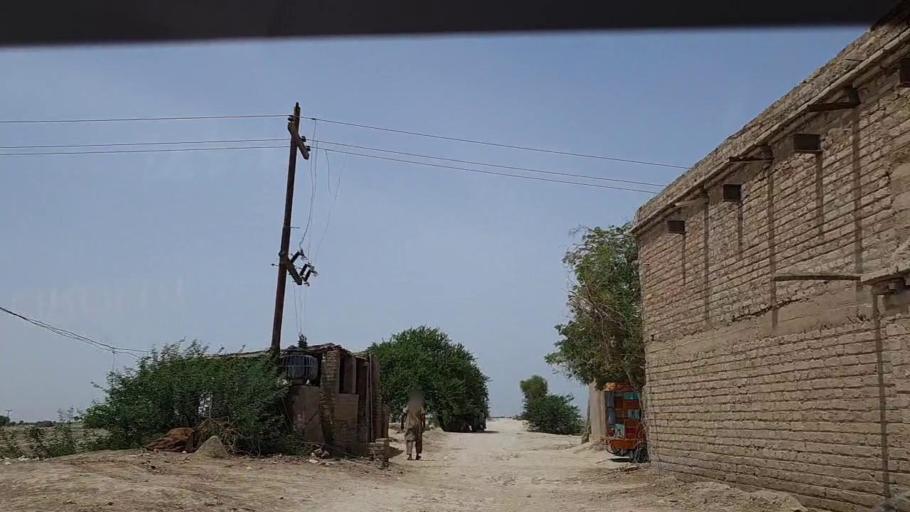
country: PK
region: Sindh
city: Johi
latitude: 26.7290
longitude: 67.6817
